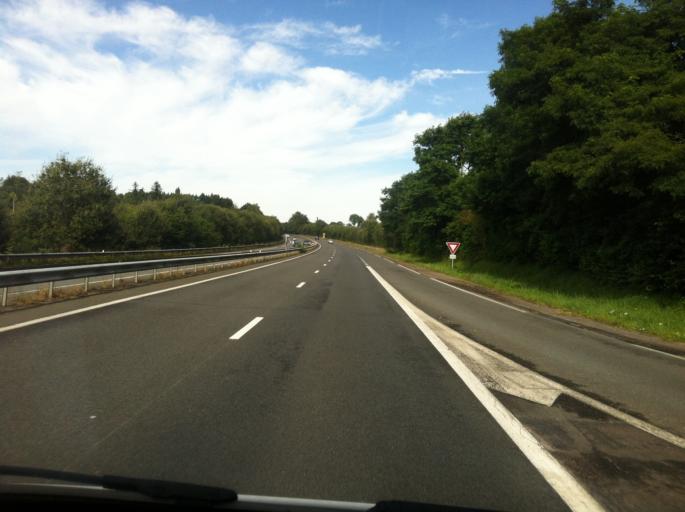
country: FR
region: Brittany
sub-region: Departement des Cotes-d'Armor
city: Pedernec
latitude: 48.5713
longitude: -3.2609
